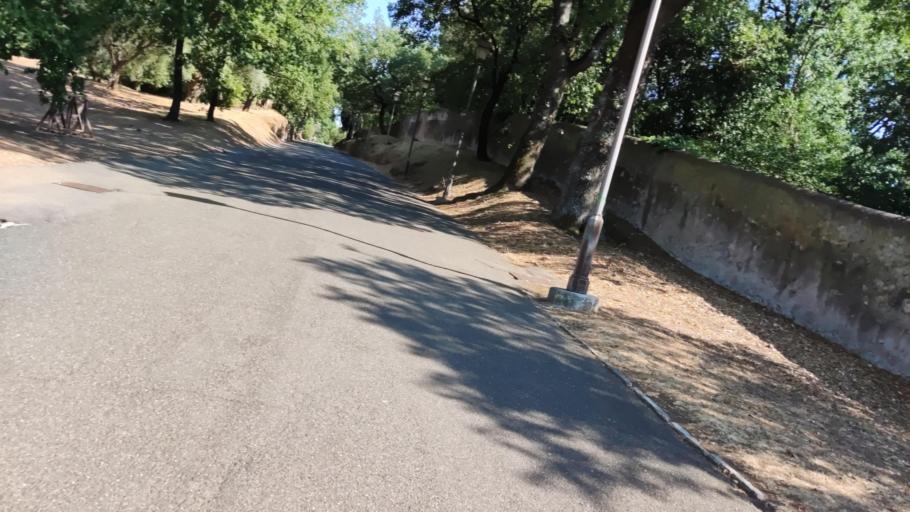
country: IT
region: Latium
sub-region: Citta metropolitana di Roma Capitale
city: Villa Adriana
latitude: 41.9445
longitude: 12.7724
